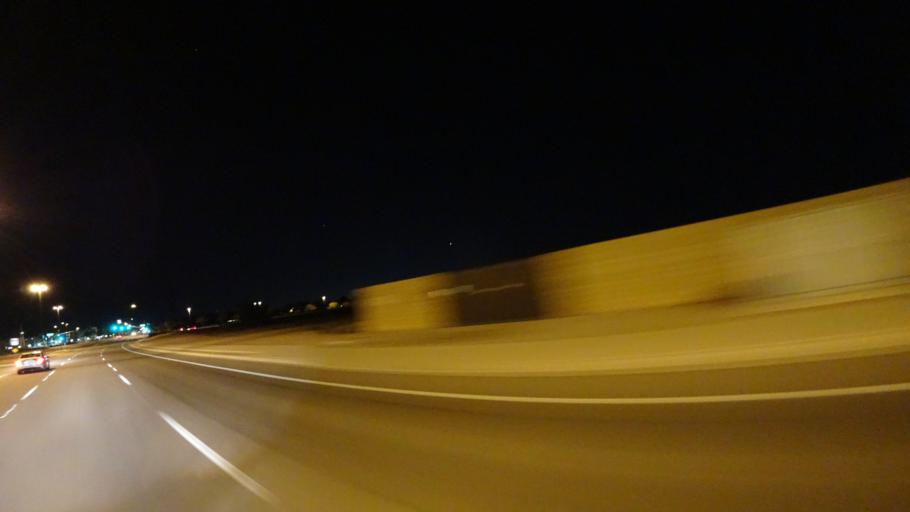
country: US
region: Arizona
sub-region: Maricopa County
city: Gilbert
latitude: 33.3215
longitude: -111.7403
